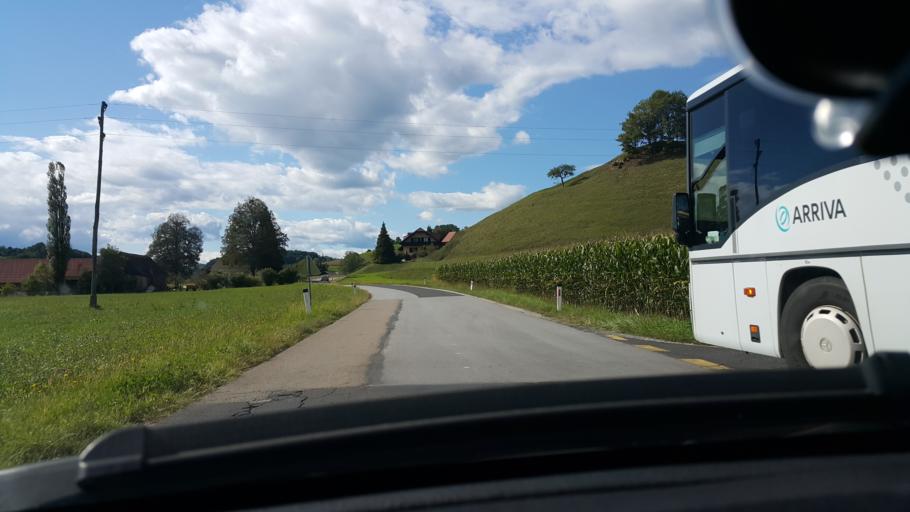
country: SI
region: Kungota
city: Zgornja Kungota
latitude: 46.6444
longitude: 15.5787
